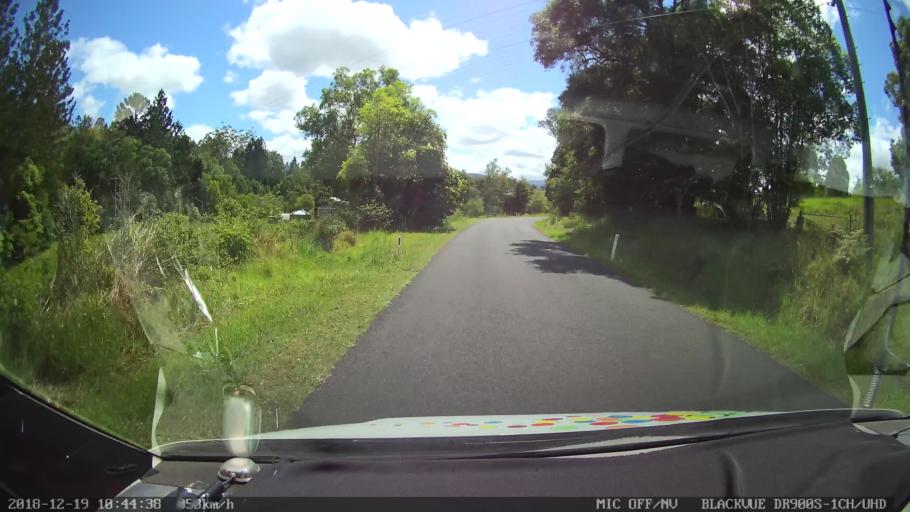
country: AU
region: New South Wales
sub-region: Lismore Municipality
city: Nimbin
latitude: -28.5953
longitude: 153.1826
